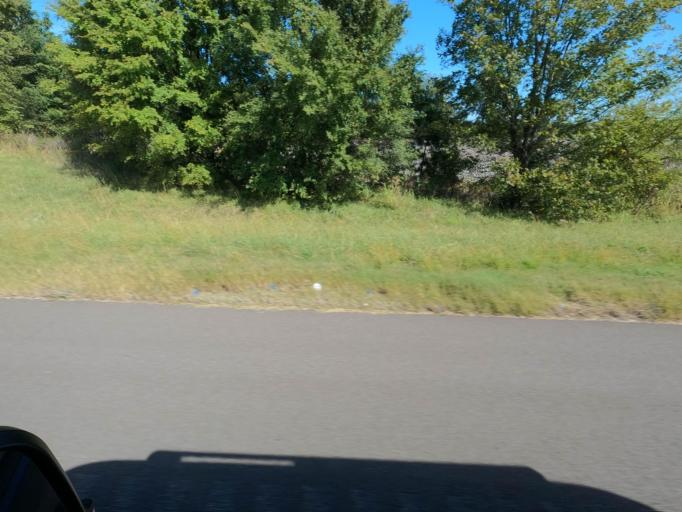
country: US
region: Tennessee
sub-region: Lauderdale County
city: Halls
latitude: 35.9343
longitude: -89.2905
